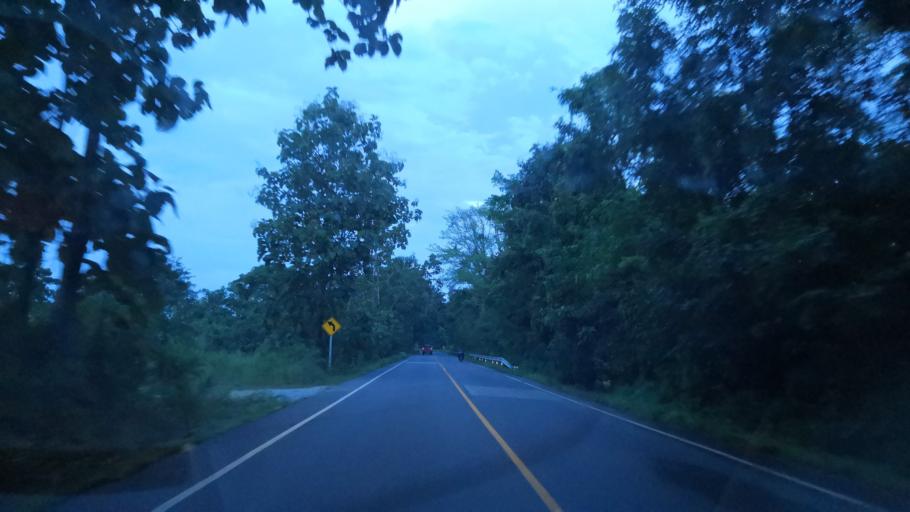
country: TH
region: Chiang Rai
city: Wiang Chai
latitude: 19.9382
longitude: 99.9176
